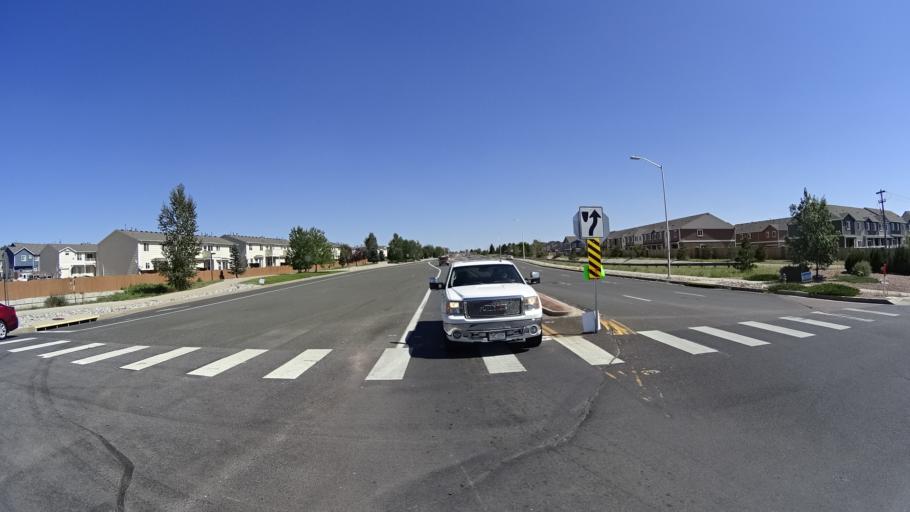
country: US
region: Colorado
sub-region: El Paso County
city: Stratmoor
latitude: 38.7890
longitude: -104.7389
